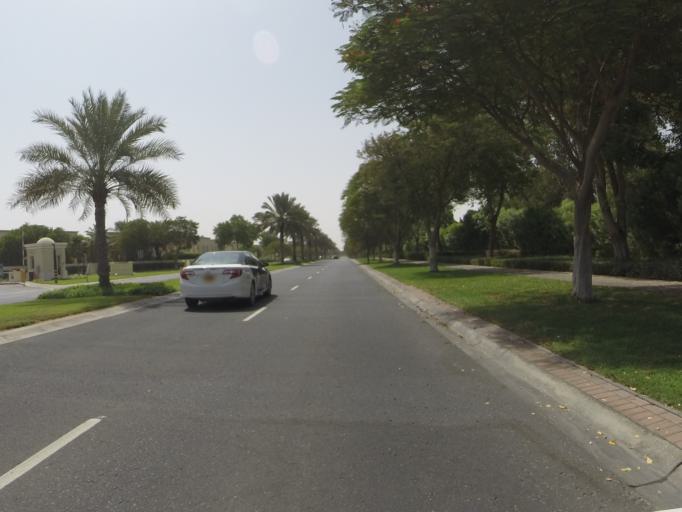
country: AE
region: Dubai
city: Dubai
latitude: 25.0604
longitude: 55.1597
